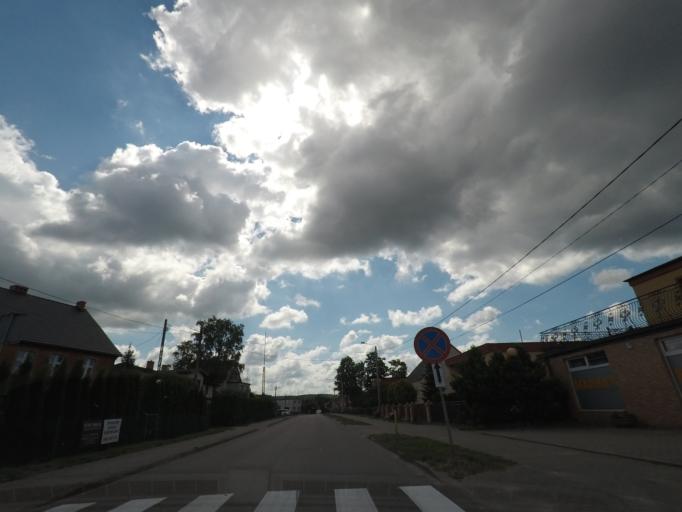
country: PL
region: Pomeranian Voivodeship
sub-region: Powiat wejherowski
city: Leczyce
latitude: 54.5855
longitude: 17.8627
